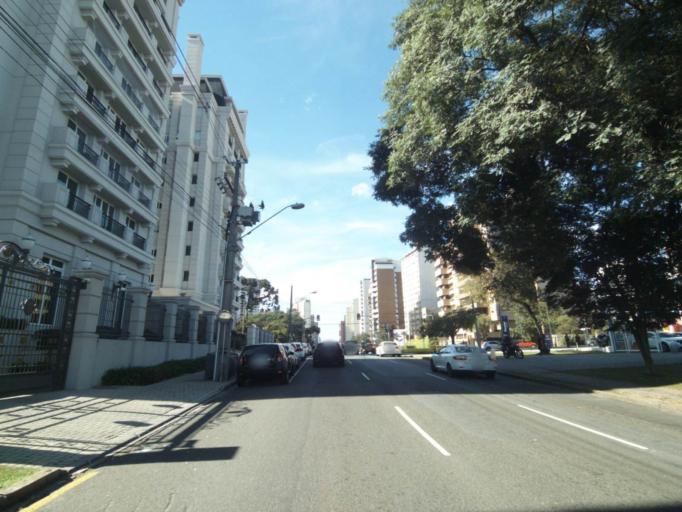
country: BR
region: Parana
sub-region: Curitiba
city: Curitiba
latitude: -25.4493
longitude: -49.2929
